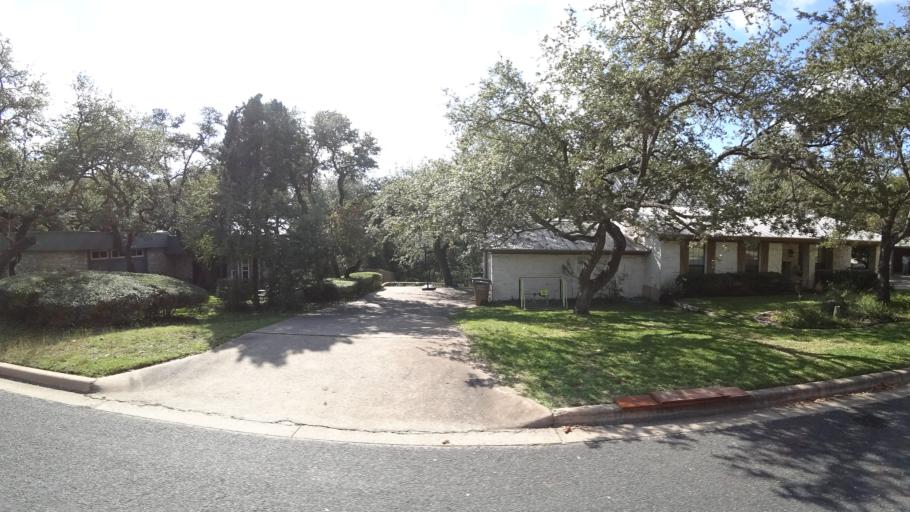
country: US
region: Texas
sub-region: Williamson County
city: Anderson Mill
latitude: 30.4289
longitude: -97.8063
